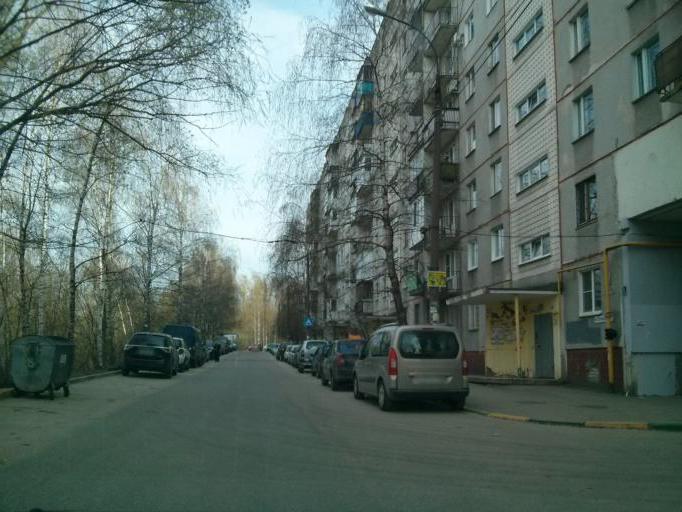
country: RU
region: Nizjnij Novgorod
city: Afonino
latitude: 56.2992
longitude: 44.0649
